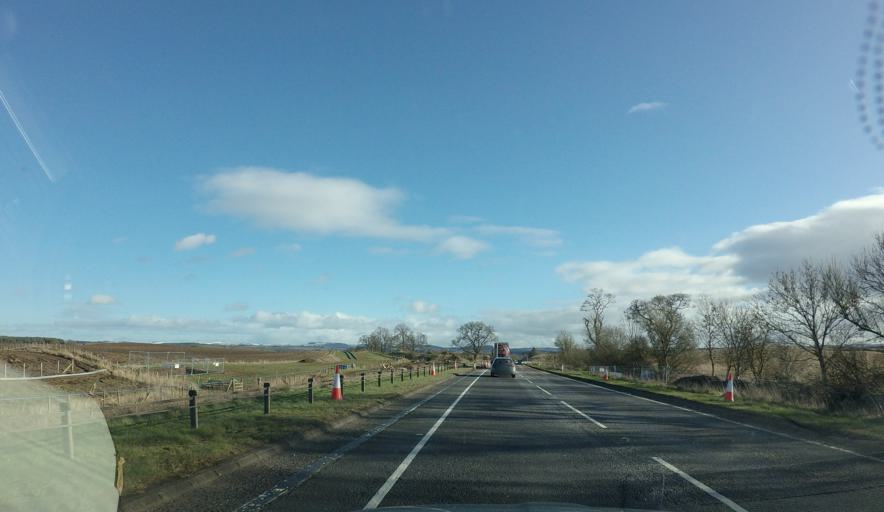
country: GB
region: Scotland
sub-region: Perth and Kinross
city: Bankfoot
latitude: 56.4777
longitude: -3.4906
